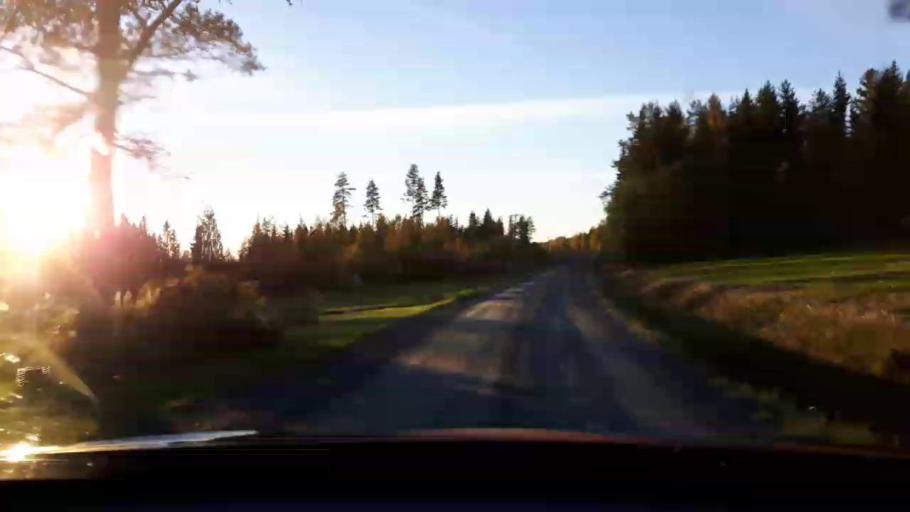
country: SE
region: Jaemtland
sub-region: Krokoms Kommun
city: Krokom
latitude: 63.4270
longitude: 14.4521
